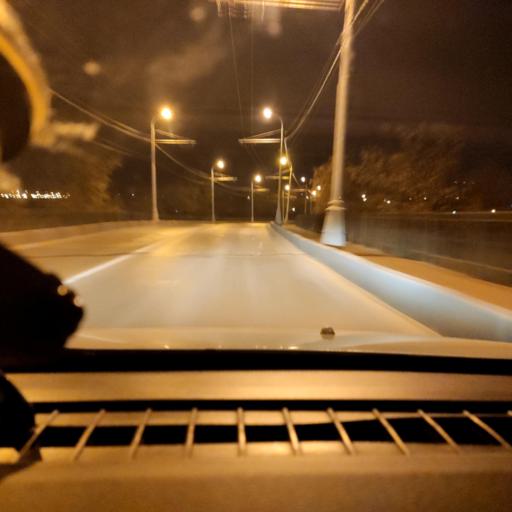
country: RU
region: Samara
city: Rozhdestveno
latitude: 53.1714
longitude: 50.0752
